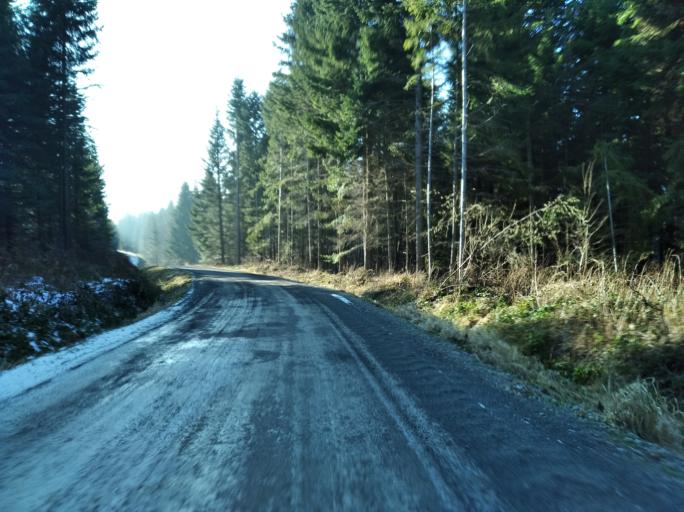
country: PL
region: Subcarpathian Voivodeship
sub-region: Powiat rzeszowski
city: Straszydle
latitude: 49.8736
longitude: 21.9777
